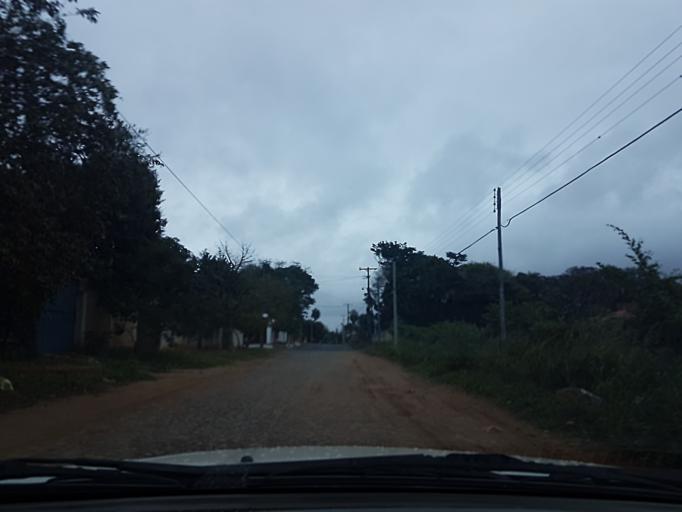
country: PY
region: Central
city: Colonia Mariano Roque Alonso
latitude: -25.2112
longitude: -57.5252
